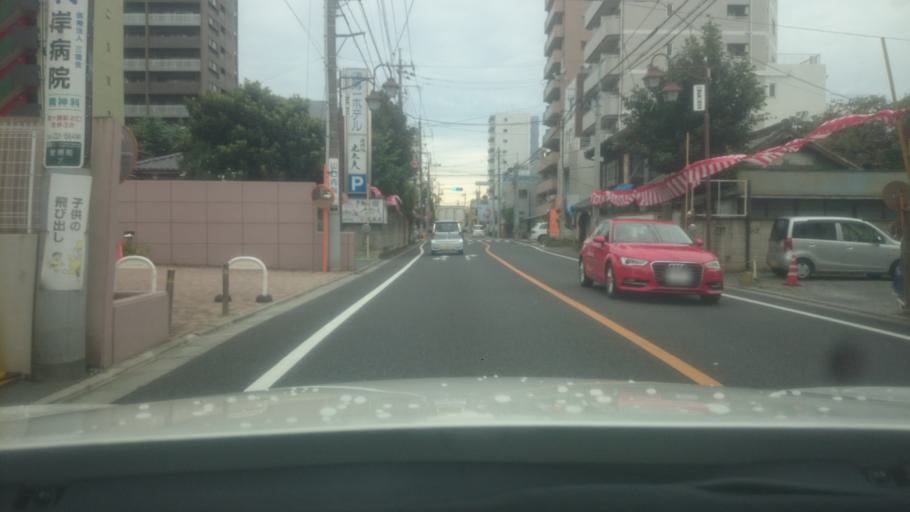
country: JP
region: Saitama
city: Kawagoe
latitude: 35.9065
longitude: 139.4867
